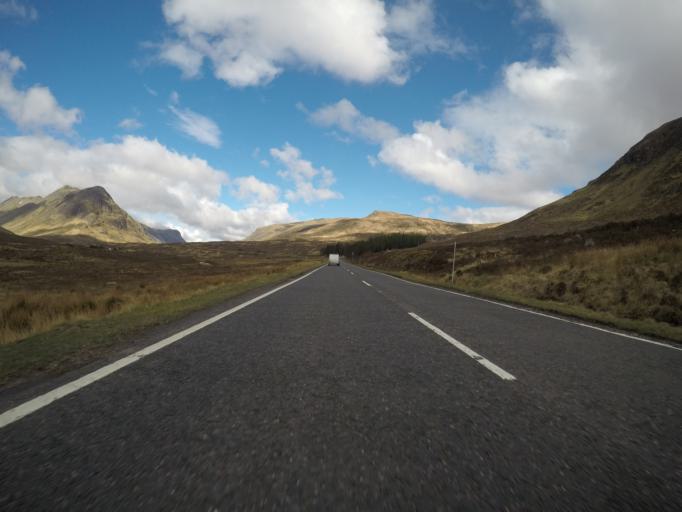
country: GB
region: Scotland
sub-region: Highland
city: Spean Bridge
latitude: 56.6628
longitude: -4.8964
